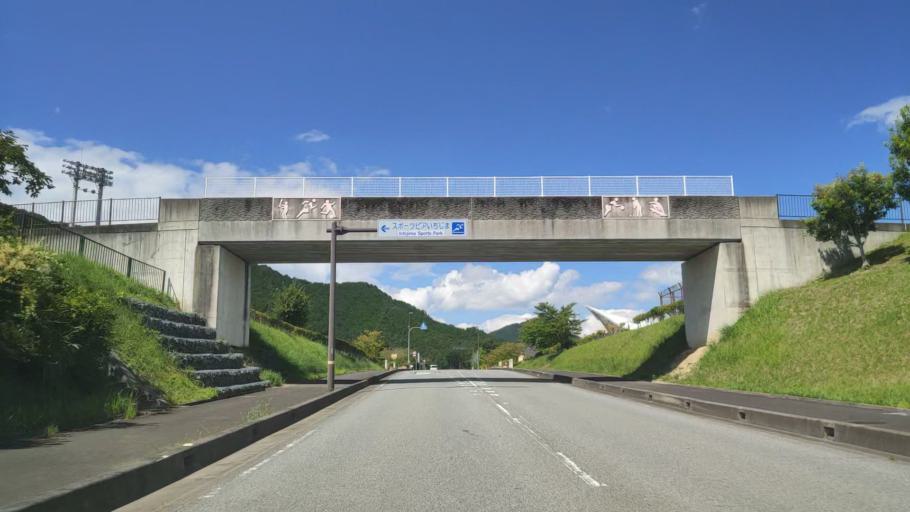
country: JP
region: Kyoto
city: Fukuchiyama
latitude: 35.2366
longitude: 135.1255
